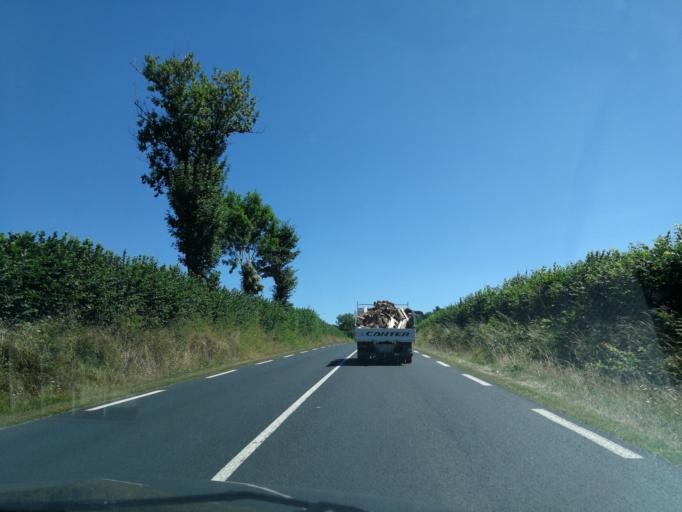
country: FR
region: Auvergne
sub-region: Departement du Cantal
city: Naucelles
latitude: 44.9358
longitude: 2.4020
